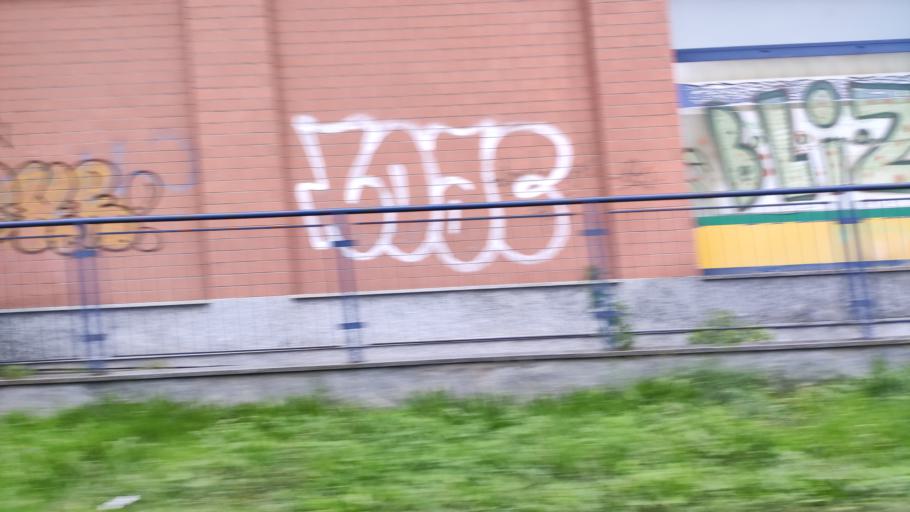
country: IT
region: Piedmont
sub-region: Provincia di Torino
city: Settimo Torinese
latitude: 45.1421
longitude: 7.7677
